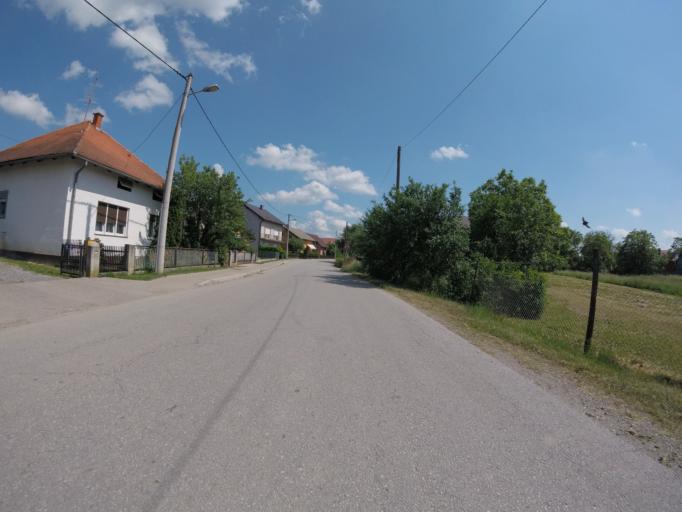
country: HR
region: Zagrebacka
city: Kuce
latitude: 45.6773
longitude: 16.1414
